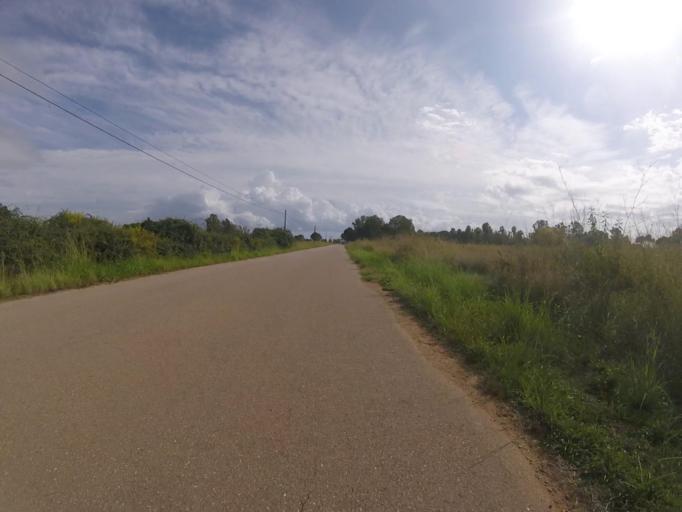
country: ES
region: Valencia
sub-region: Provincia de Castello
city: Orpesa/Oropesa del Mar
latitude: 40.1308
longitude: 0.1600
